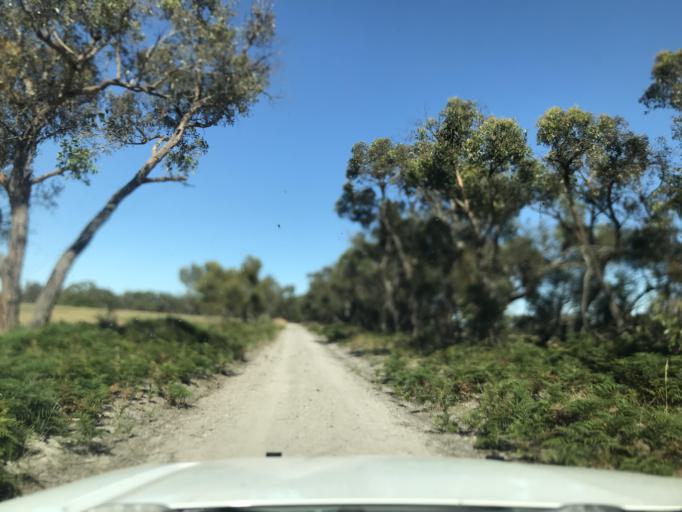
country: AU
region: South Australia
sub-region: Wattle Range
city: Penola
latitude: -37.0810
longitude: 141.3889
